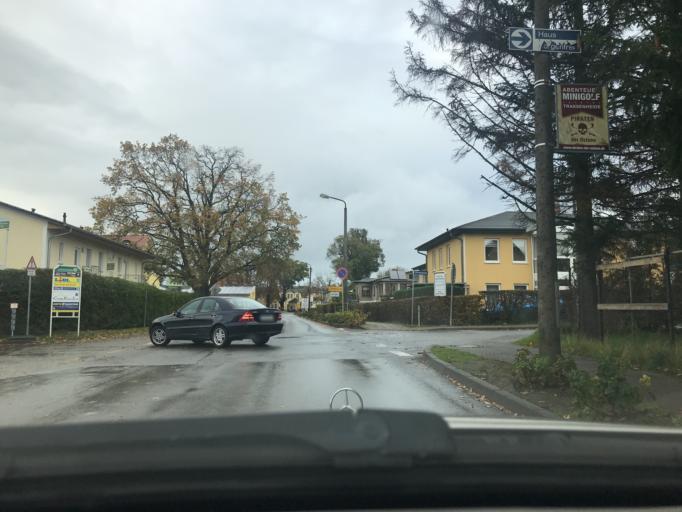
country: DE
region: Mecklenburg-Vorpommern
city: Ostseebad Zinnowitz
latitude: 54.0752
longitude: 13.9091
